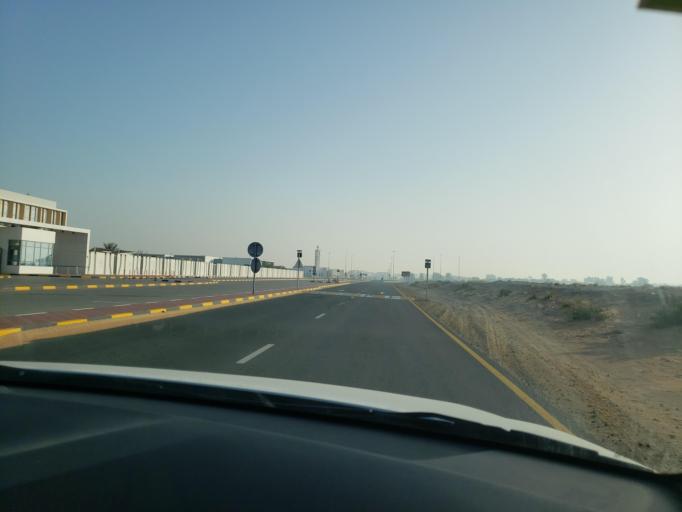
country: AE
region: Umm al Qaywayn
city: Umm al Qaywayn
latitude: 25.4670
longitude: 55.6122
